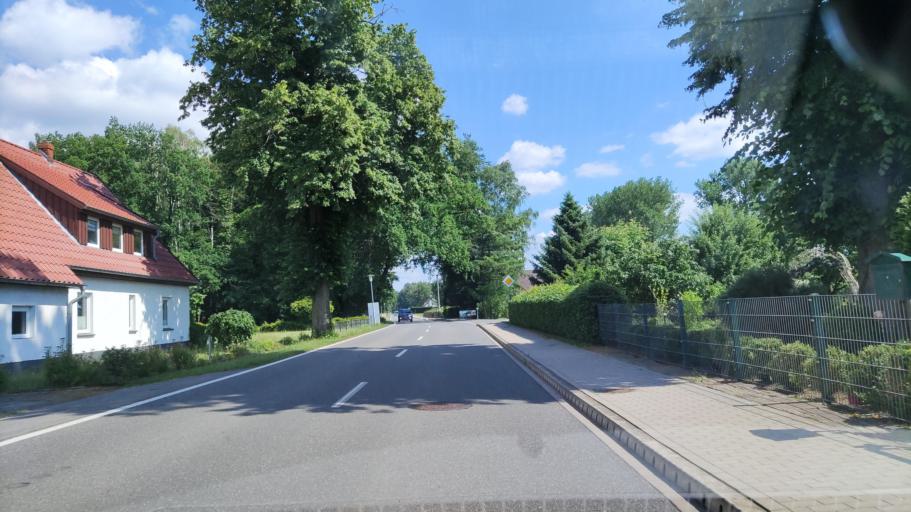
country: DE
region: Mecklenburg-Vorpommern
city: Lubtheen
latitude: 53.2617
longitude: 11.1055
